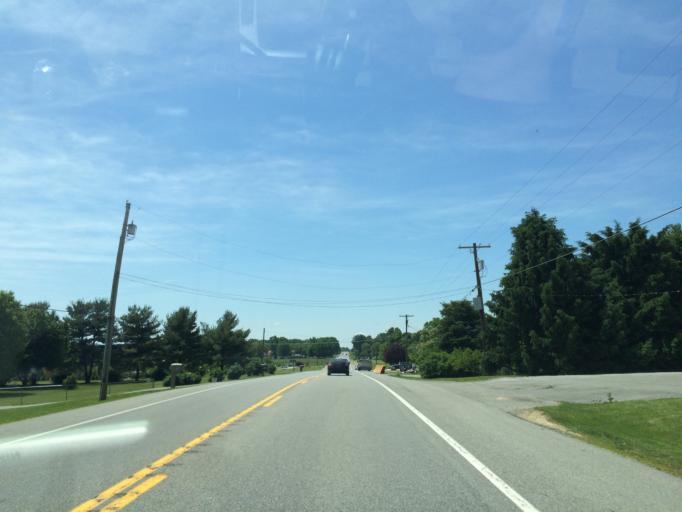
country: US
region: Maryland
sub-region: Washington County
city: Saint James
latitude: 39.5222
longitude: -77.7435
